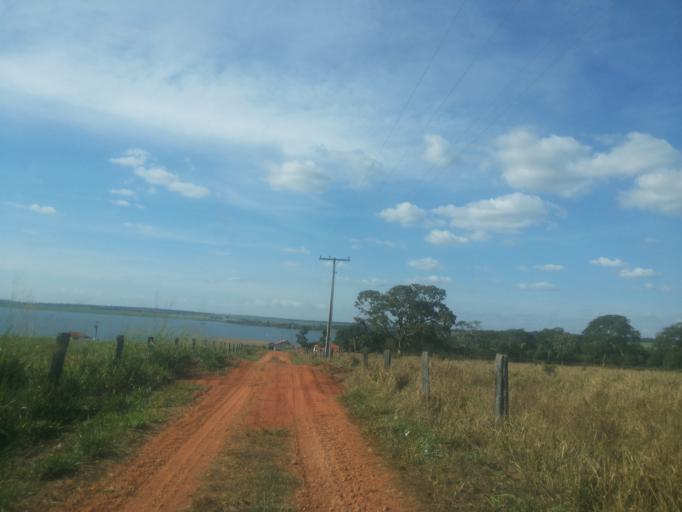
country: BR
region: Minas Gerais
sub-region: Santa Vitoria
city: Santa Vitoria
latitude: -19.0040
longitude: -50.3977
